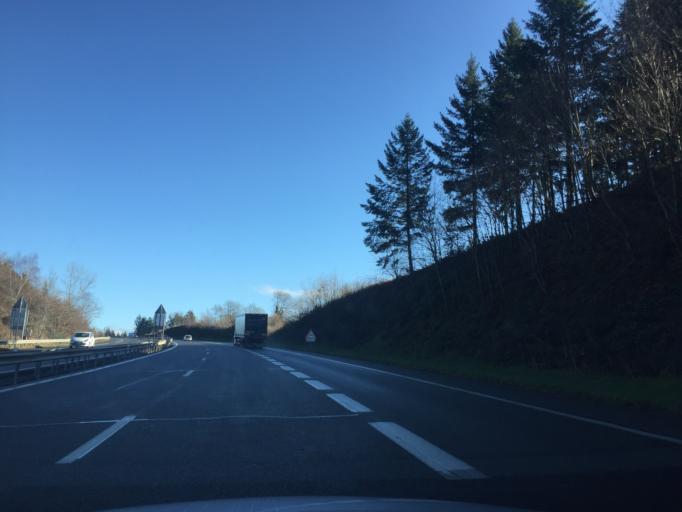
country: FR
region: Auvergne
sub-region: Departement du Puy-de-Dome
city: Thiers
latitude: 45.8650
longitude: 3.5482
